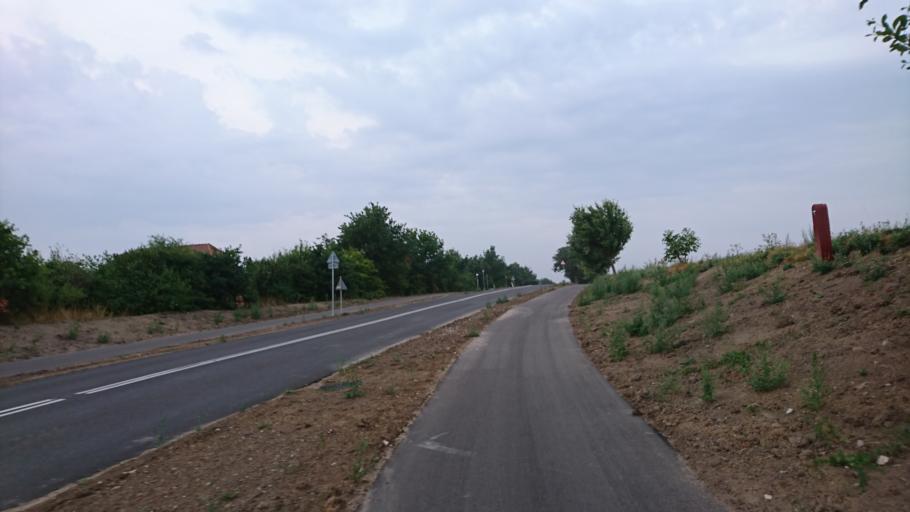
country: DK
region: Capital Region
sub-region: Ballerup Kommune
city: Malov
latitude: 55.7570
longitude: 12.3091
